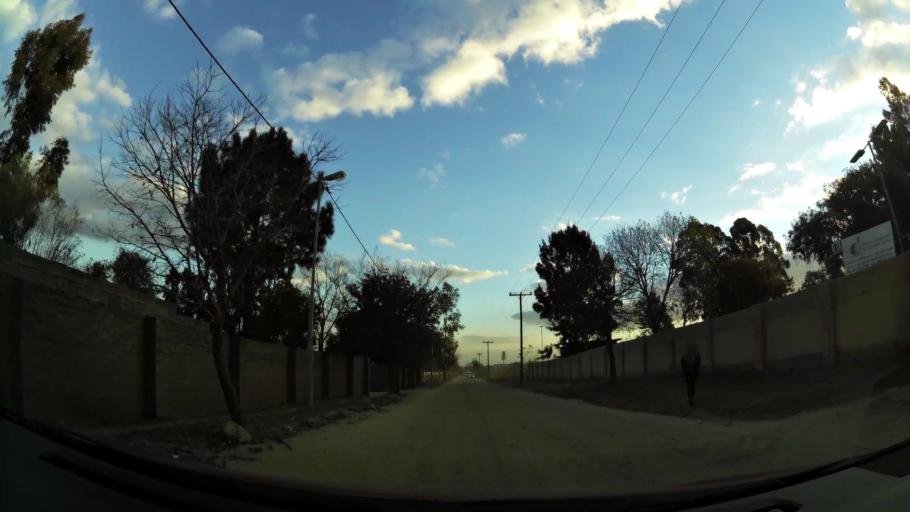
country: ZA
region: Gauteng
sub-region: City of Johannesburg Metropolitan Municipality
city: Midrand
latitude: -25.9992
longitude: 28.1477
